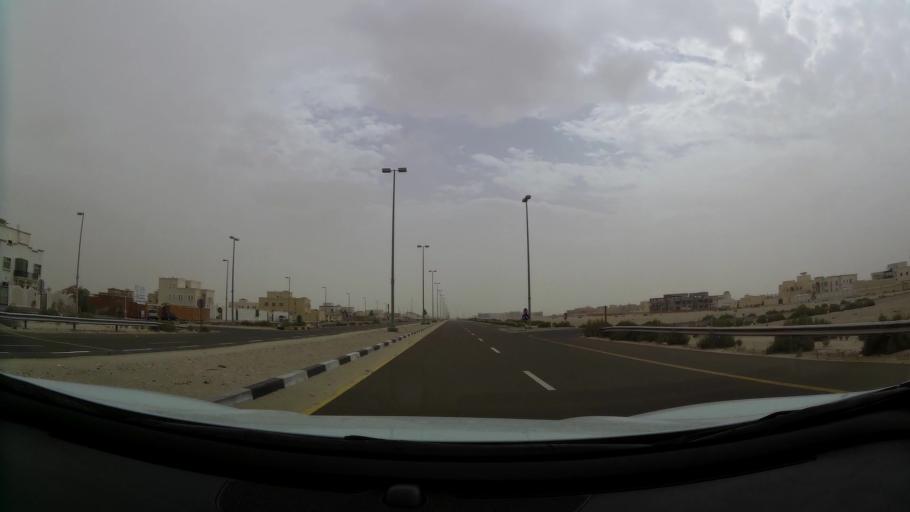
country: AE
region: Abu Dhabi
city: Abu Dhabi
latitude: 24.3637
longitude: 54.6959
